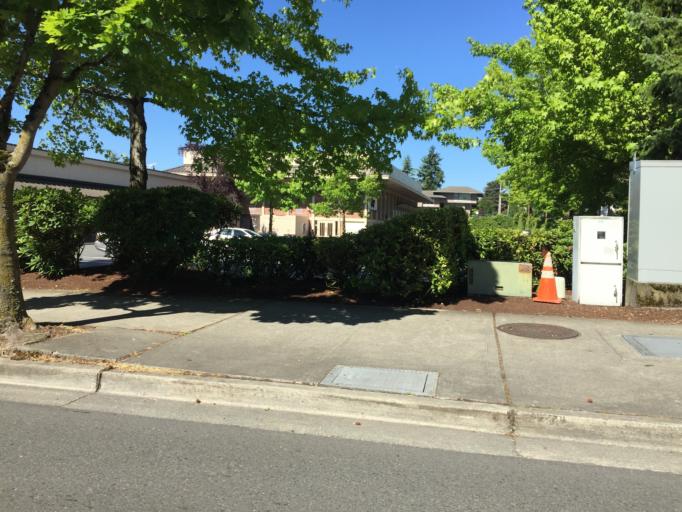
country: US
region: Washington
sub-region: King County
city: Bellevue
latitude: 47.6191
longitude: -122.2044
